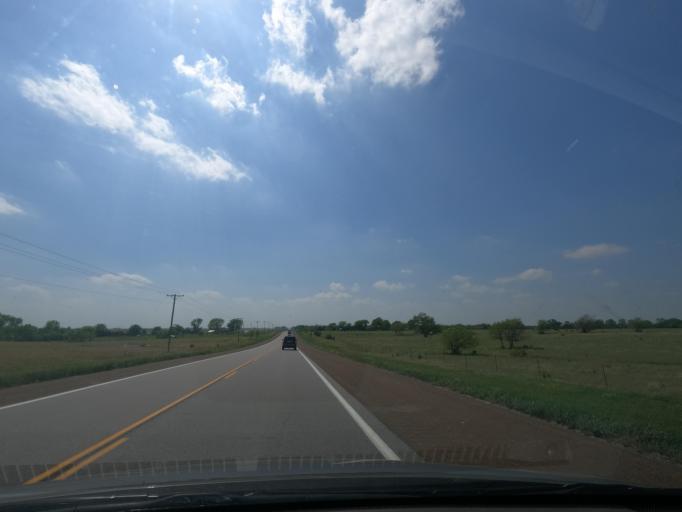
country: US
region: Kansas
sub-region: Butler County
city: El Dorado
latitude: 37.6795
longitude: -96.8215
